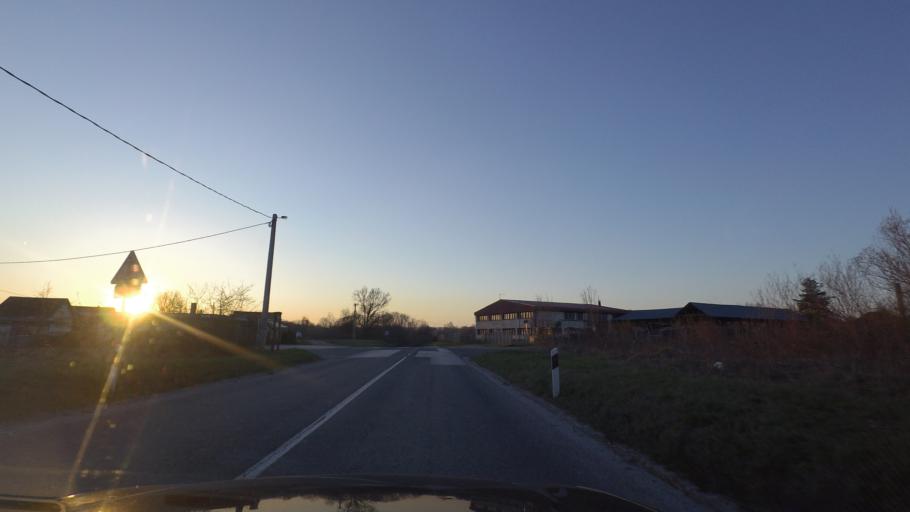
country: HR
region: Sisacko-Moslavacka
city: Gvozd
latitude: 45.3382
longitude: 15.9009
